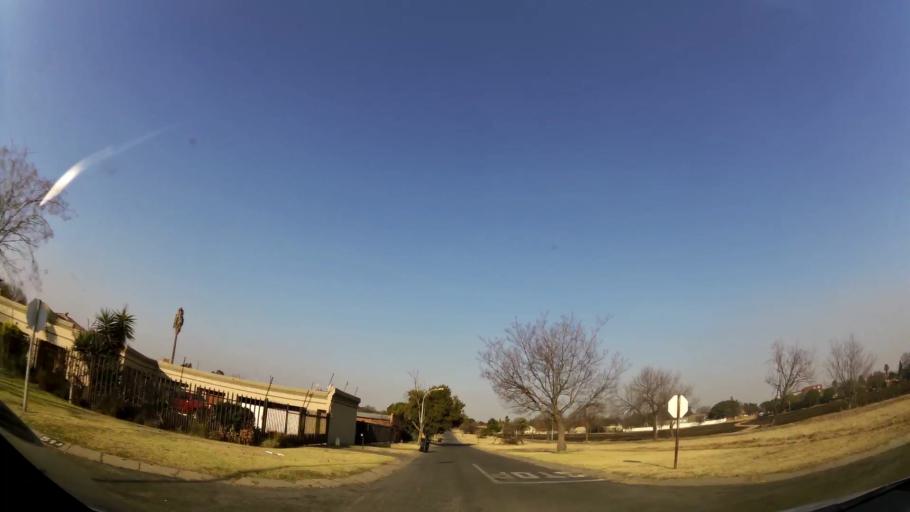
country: ZA
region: Gauteng
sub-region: Ekurhuleni Metropolitan Municipality
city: Springs
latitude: -26.2526
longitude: 28.3903
